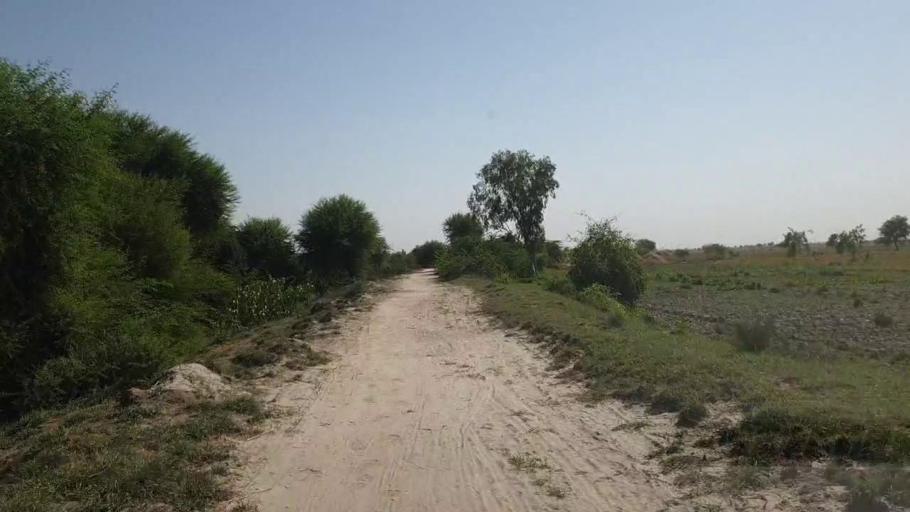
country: PK
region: Sindh
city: Kadhan
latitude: 24.6321
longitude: 68.9927
